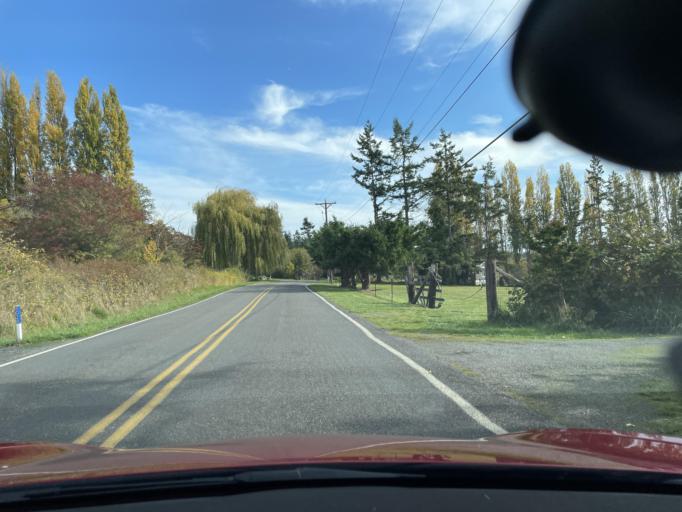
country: US
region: Washington
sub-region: San Juan County
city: Friday Harbor
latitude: 48.5229
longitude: -123.0156
